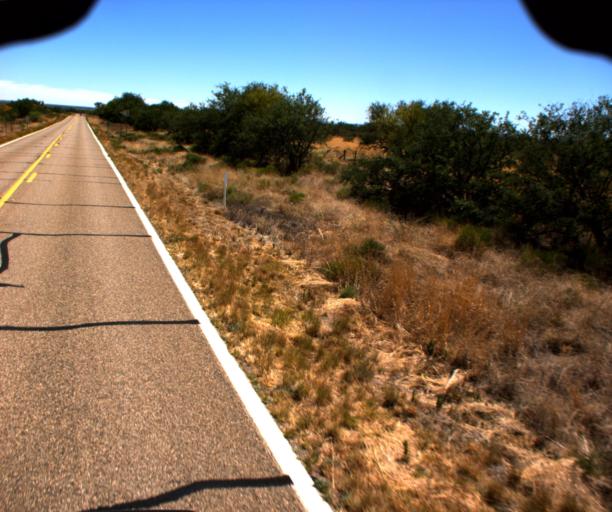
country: US
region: Arizona
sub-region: Pima County
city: Arivaca Junction
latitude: 31.6733
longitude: -111.4878
